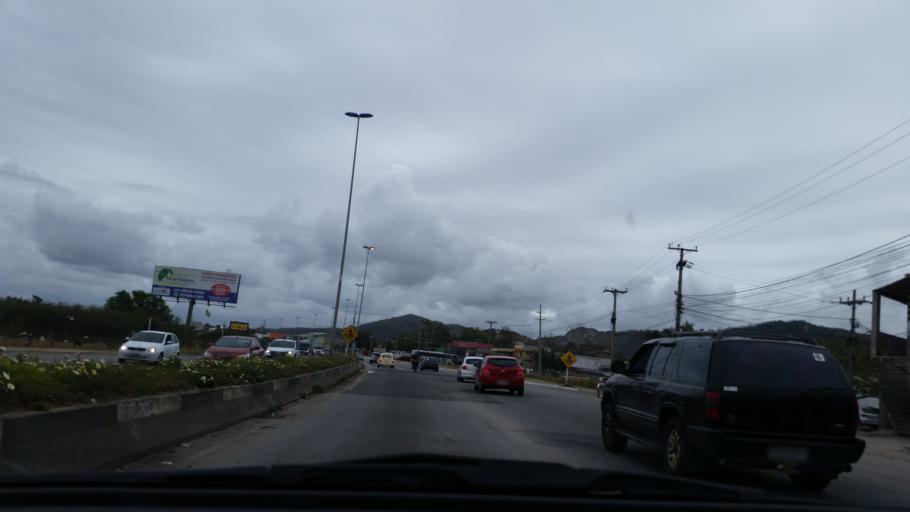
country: BR
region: Rio de Janeiro
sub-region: Sao Pedro Da Aldeia
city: Sao Pedro da Aldeia
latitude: -22.8509
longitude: -42.0628
